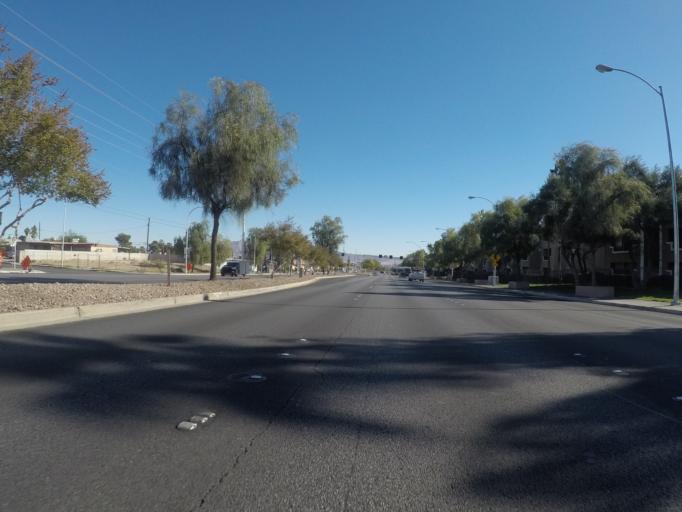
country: US
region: Nevada
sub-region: Clark County
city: Winchester
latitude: 36.1442
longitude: -115.1342
